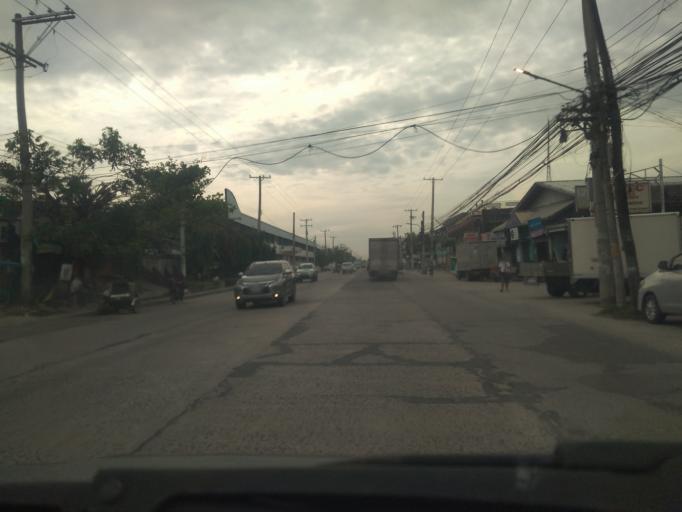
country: PH
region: Central Luzon
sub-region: Province of Pampanga
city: San Fernando
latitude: 15.0205
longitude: 120.6996
